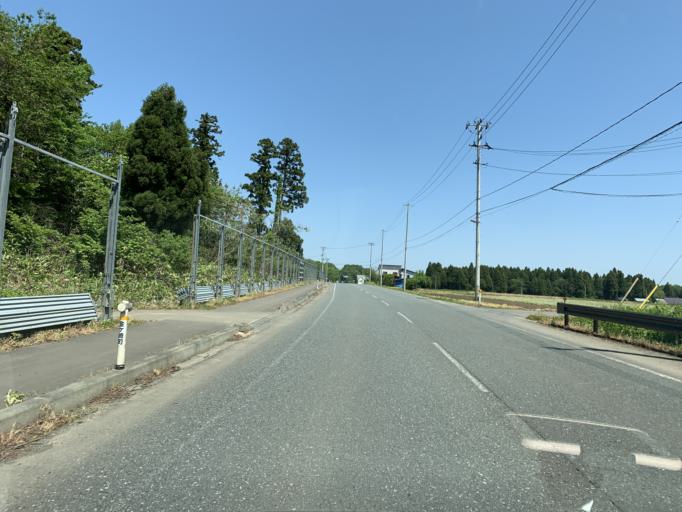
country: JP
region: Iwate
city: Kitakami
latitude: 39.2475
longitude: 141.0663
